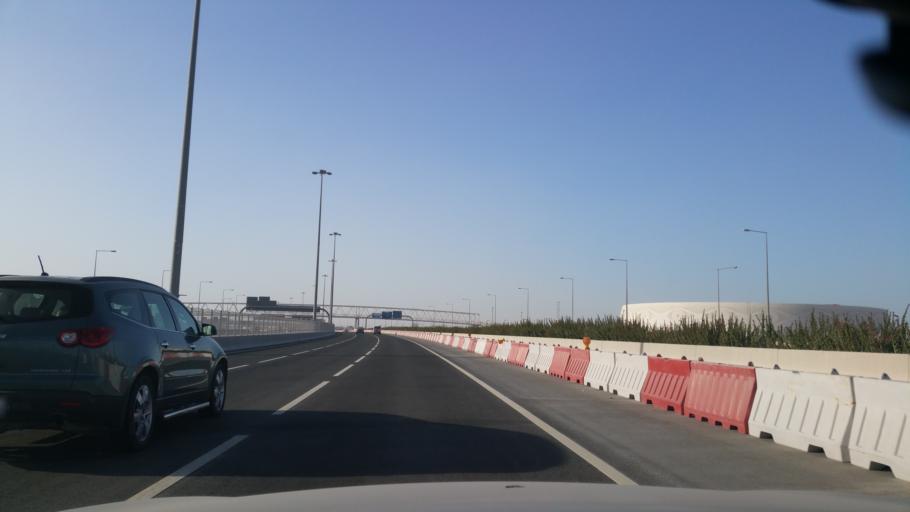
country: QA
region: Baladiyat ad Dawhah
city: Doha
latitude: 25.2280
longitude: 51.5323
